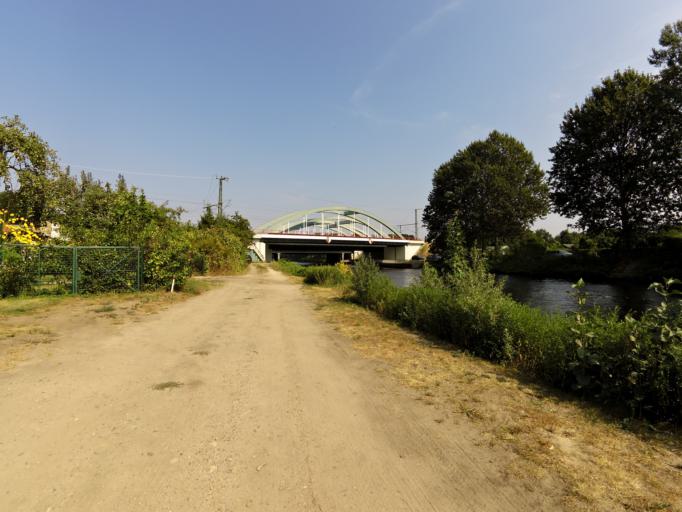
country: DE
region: Berlin
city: Adlershof
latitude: 52.4259
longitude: 13.5529
